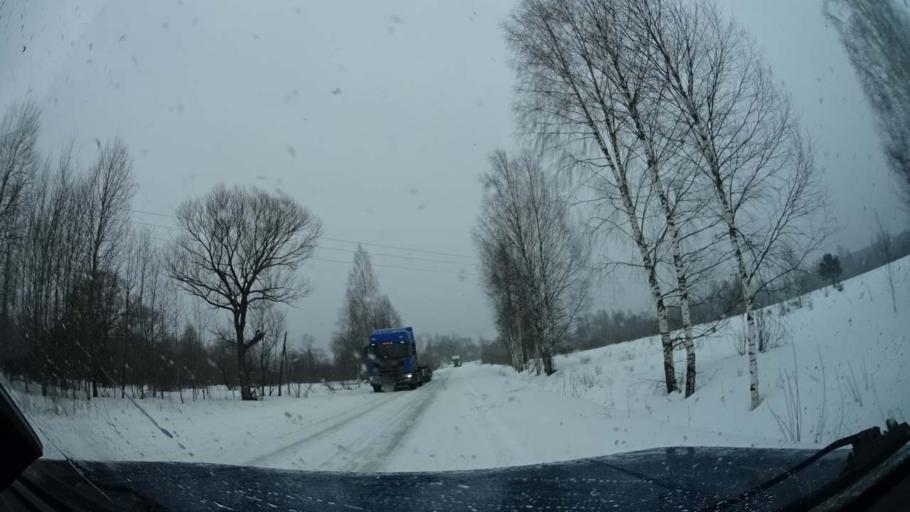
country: RU
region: Tverskaya
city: Radchenko
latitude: 56.7534
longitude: 36.5421
